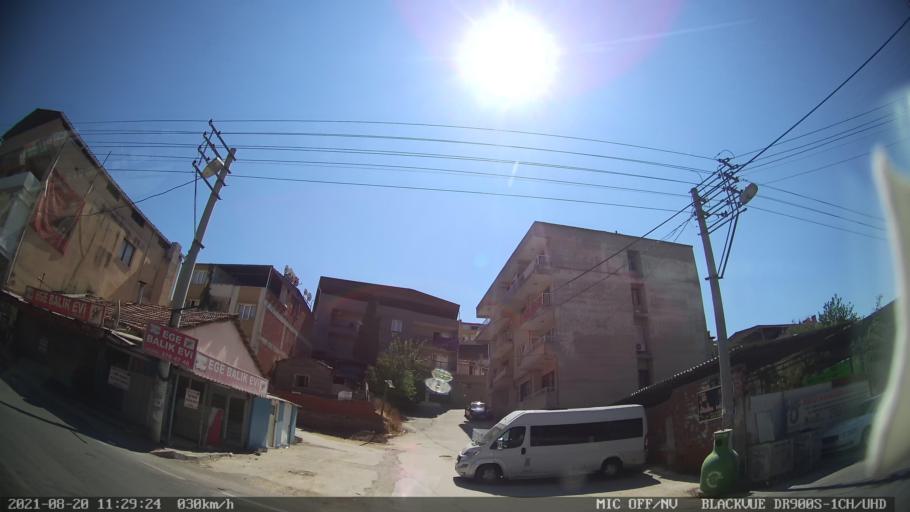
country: TR
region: Izmir
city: Karsiyaka
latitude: 38.4977
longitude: 27.0682
